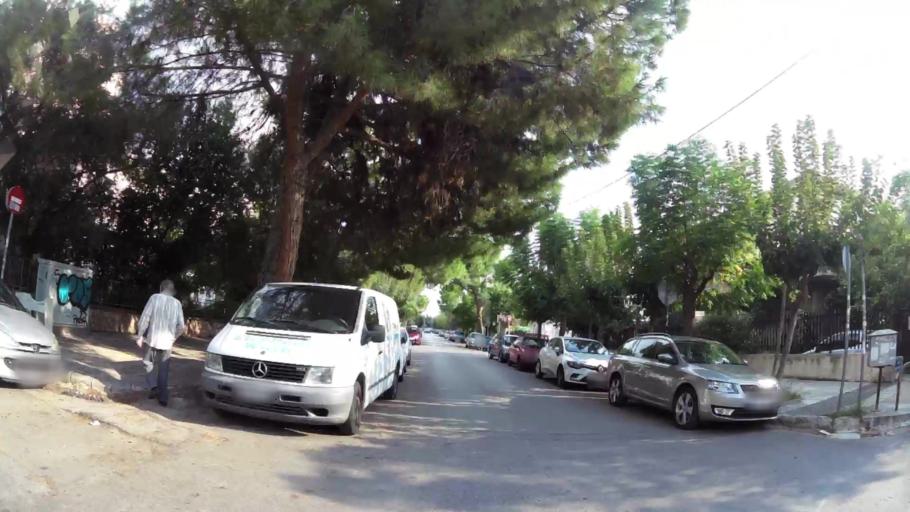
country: GR
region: Attica
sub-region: Nomarchia Athinas
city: Kallithea
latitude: 37.9473
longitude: 23.6900
